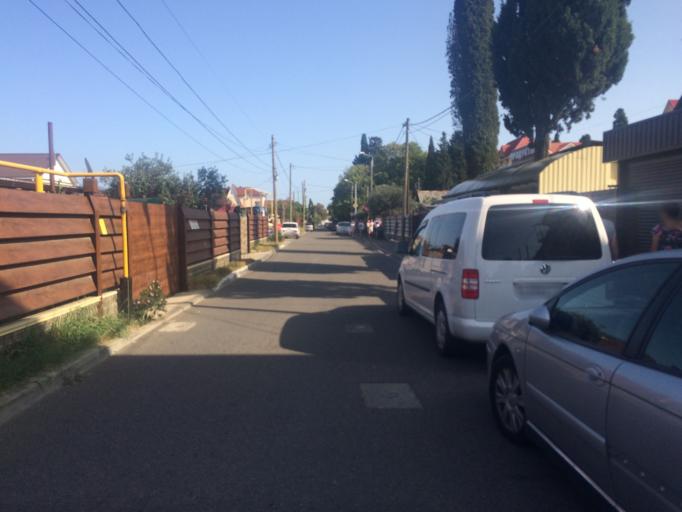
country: RU
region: Krasnodarskiy
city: Adler
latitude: 43.3950
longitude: 39.9818
